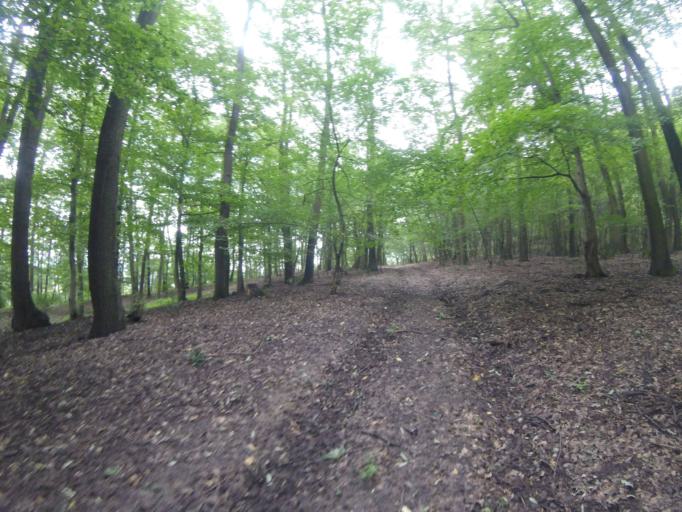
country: SK
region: Nitriansky
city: Sahy
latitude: 48.0480
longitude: 18.9764
